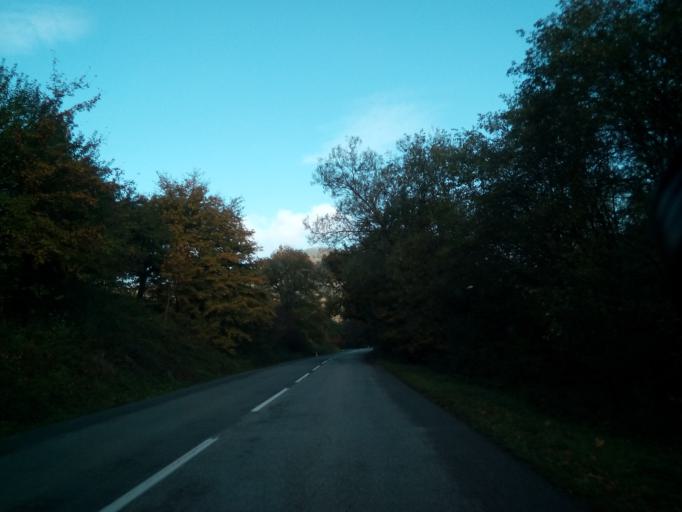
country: SK
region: Kosicky
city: Gelnica
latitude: 48.8705
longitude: 21.0029
